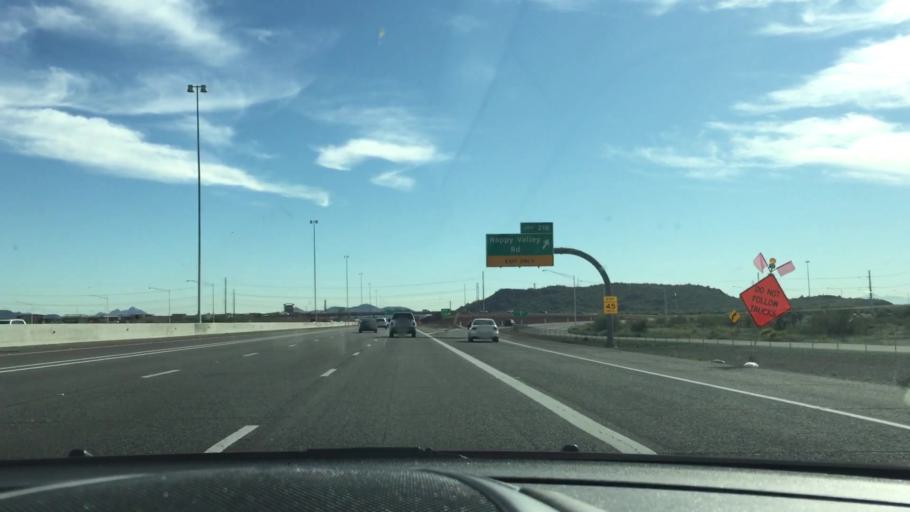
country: US
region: Arizona
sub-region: Maricopa County
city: Anthem
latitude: 33.7182
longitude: -112.1196
